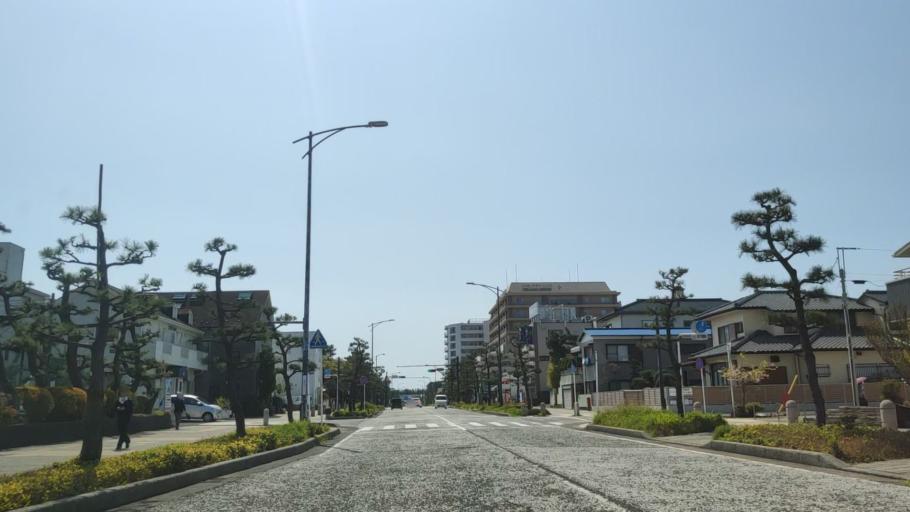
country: JP
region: Kanagawa
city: Hiratsuka
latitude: 35.3218
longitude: 139.3529
